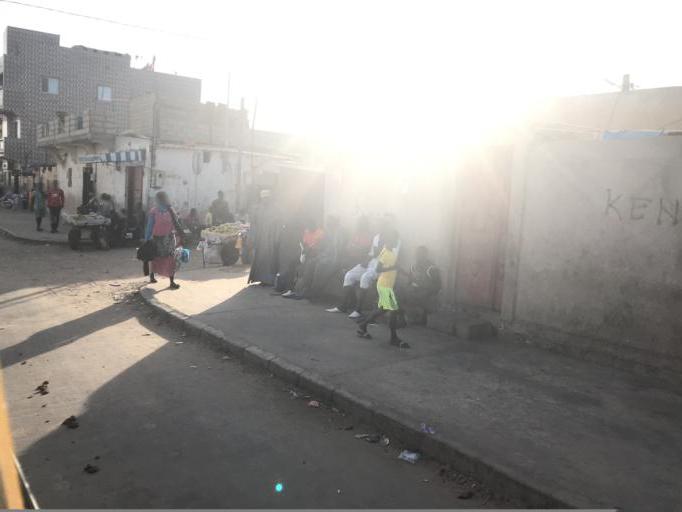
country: SN
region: Saint-Louis
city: Saint-Louis
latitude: 16.0231
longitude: -16.5074
